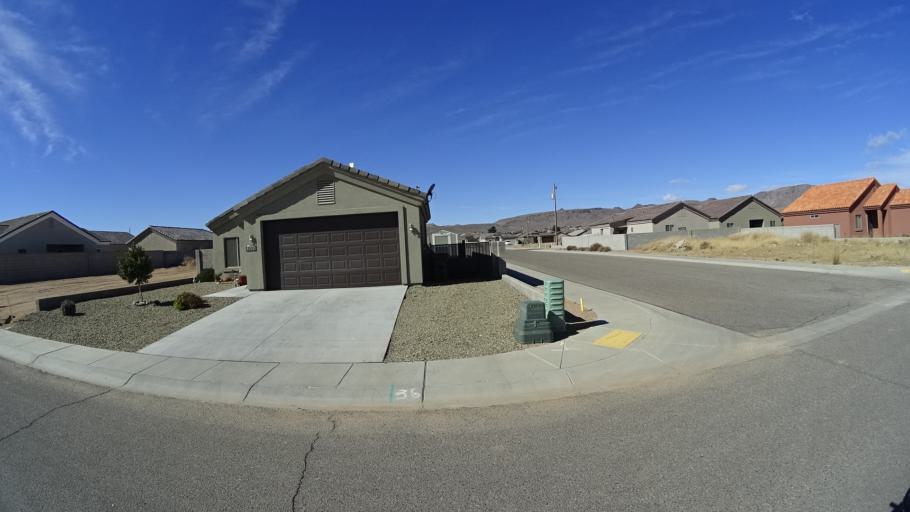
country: US
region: Arizona
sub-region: Mohave County
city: New Kingman-Butler
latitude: 35.2266
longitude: -114.0207
